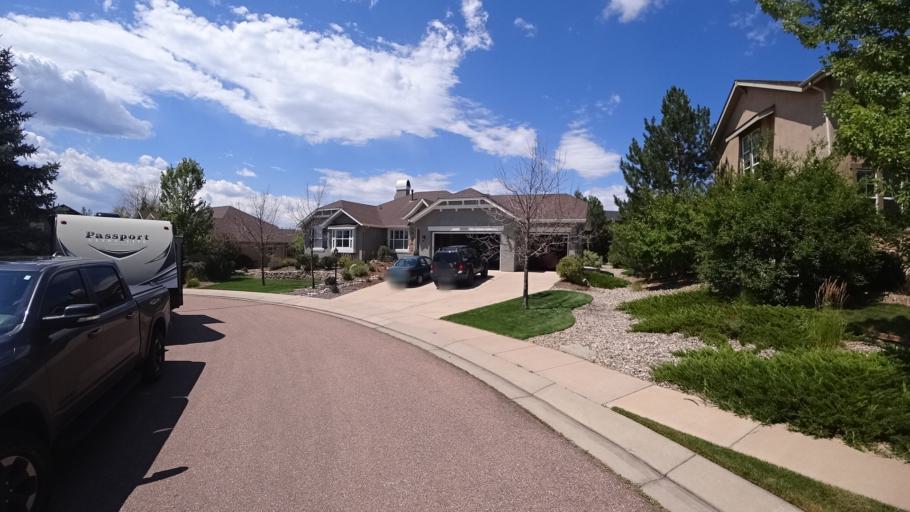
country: US
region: Colorado
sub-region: El Paso County
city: Black Forest
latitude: 38.9709
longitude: -104.7700
